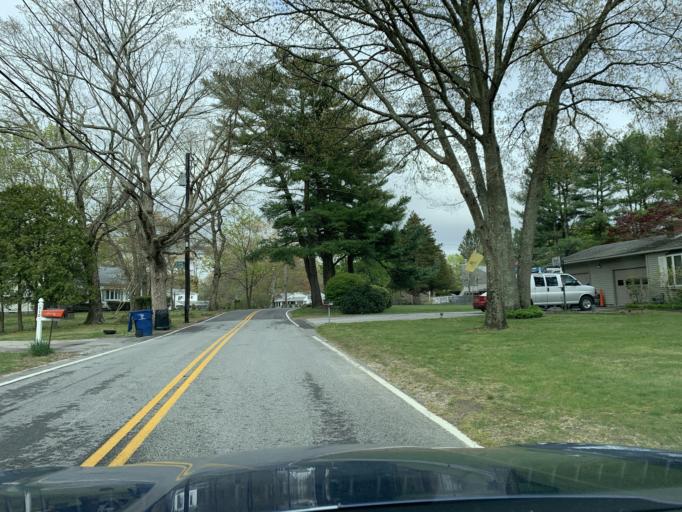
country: US
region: Rhode Island
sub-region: Washington County
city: North Kingstown
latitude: 41.6037
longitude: -71.4850
